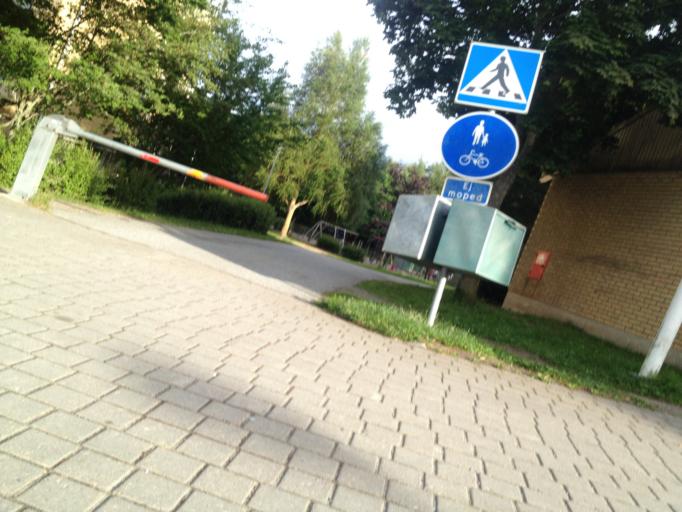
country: SE
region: Stockholm
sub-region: Sigtuna Kommun
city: Marsta
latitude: 59.6141
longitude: 17.8391
